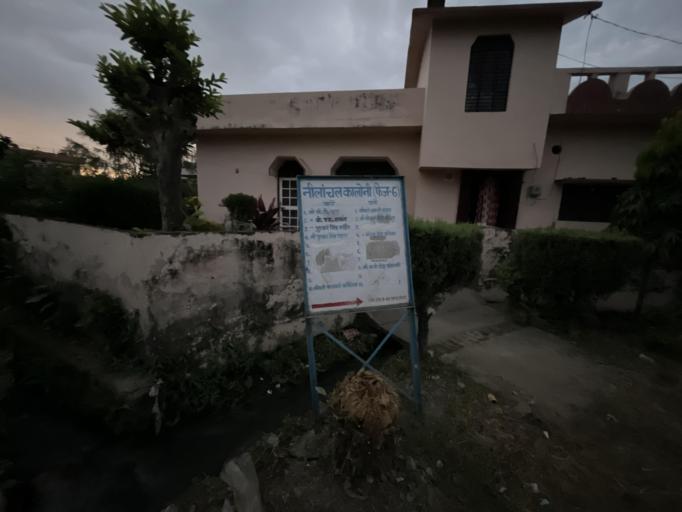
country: IN
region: Uttarakhand
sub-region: Naini Tal
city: Haldwani
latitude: 29.2010
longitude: 79.4997
